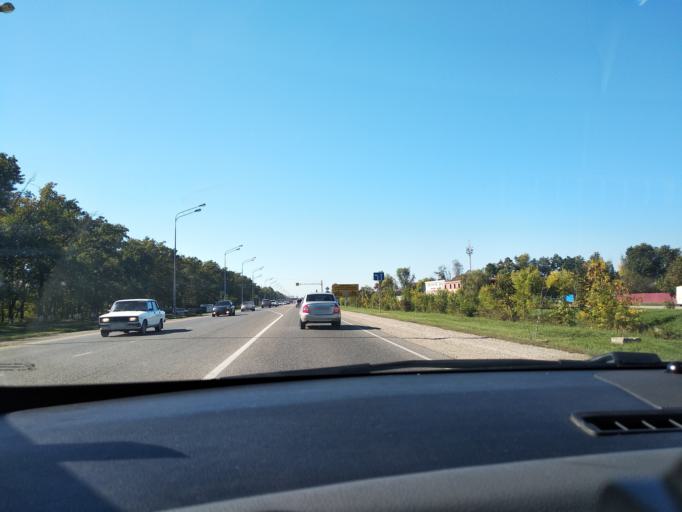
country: RU
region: Krasnodarskiy
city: Novotitarovskaya
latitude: 45.1408
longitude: 39.0393
